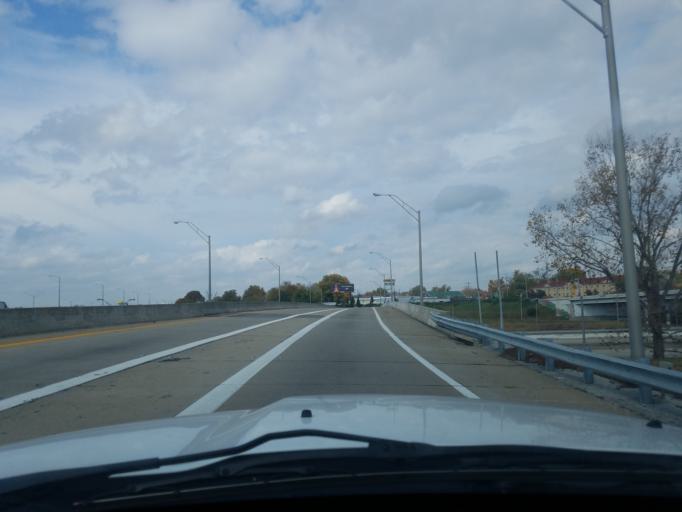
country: US
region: Kentucky
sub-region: Jefferson County
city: Audubon Park
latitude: 38.1896
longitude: -85.7279
